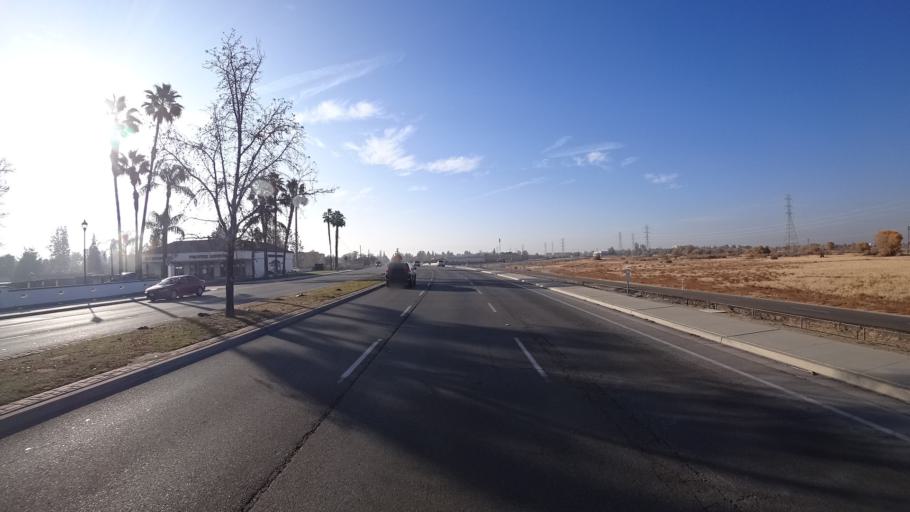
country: US
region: California
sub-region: Kern County
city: Greenacres
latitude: 35.3609
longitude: -119.0922
